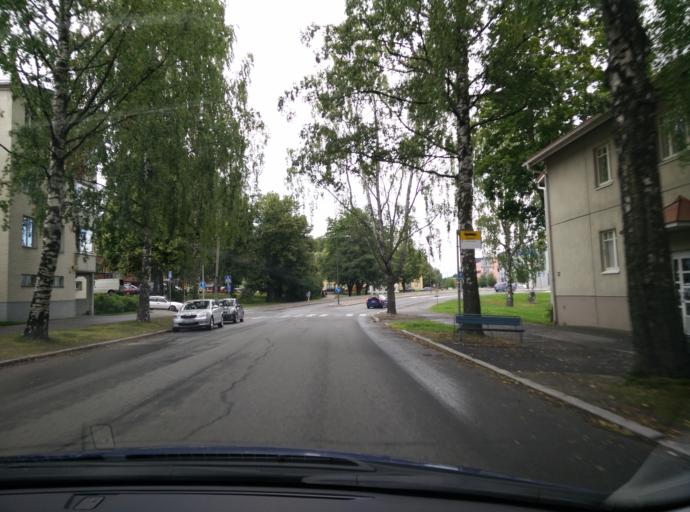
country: FI
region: Haeme
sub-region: Haemeenlinna
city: Haemeenlinna
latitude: 60.9912
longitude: 24.4564
